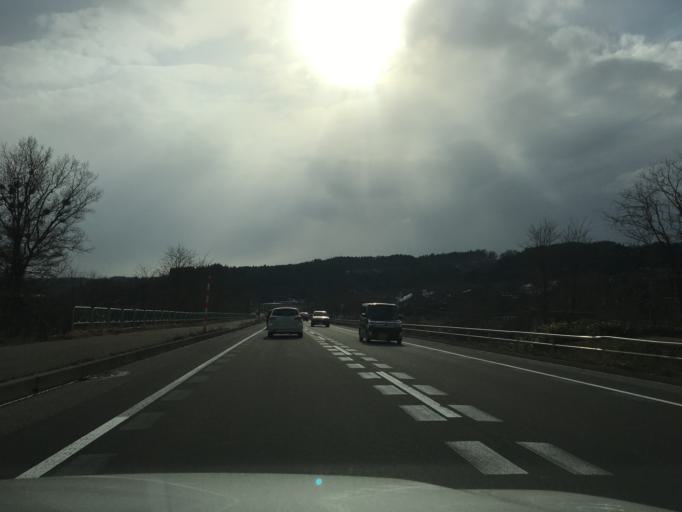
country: JP
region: Aomori
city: Namioka
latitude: 40.7684
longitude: 140.5930
